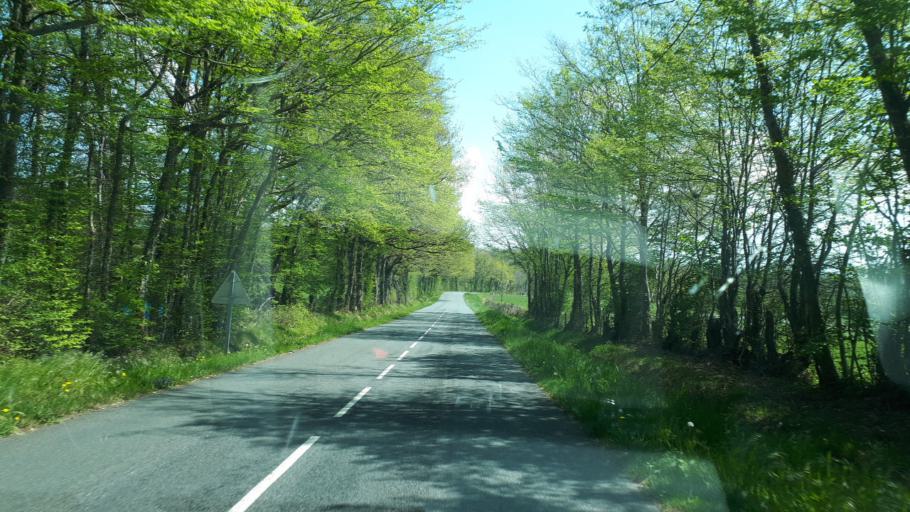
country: FR
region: Centre
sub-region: Departement du Cher
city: Henrichemont
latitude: 47.3053
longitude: 2.6456
